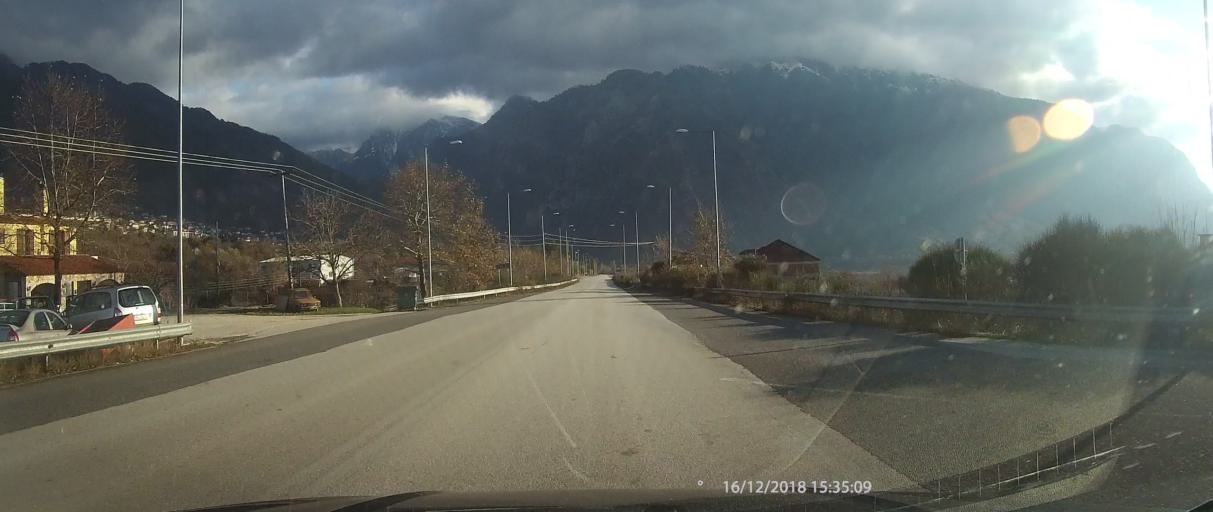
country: GR
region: Epirus
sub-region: Nomos Ioanninon
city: Konitsa
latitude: 40.0531
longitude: 20.7360
